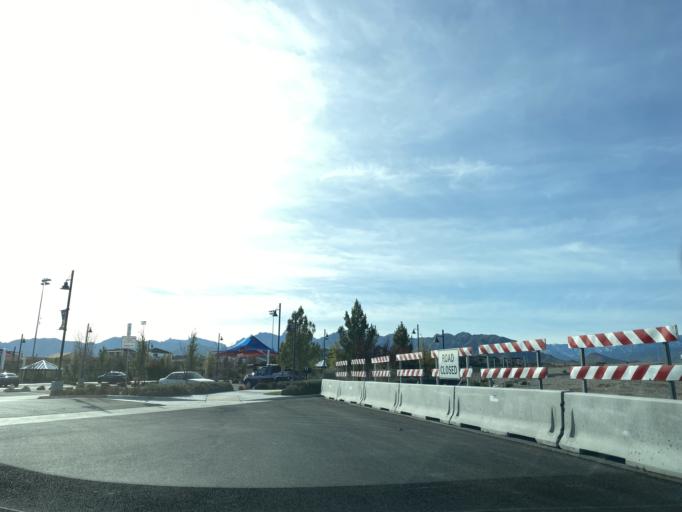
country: US
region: Nevada
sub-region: Clark County
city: Summerlin South
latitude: 36.3141
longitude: -115.3161
